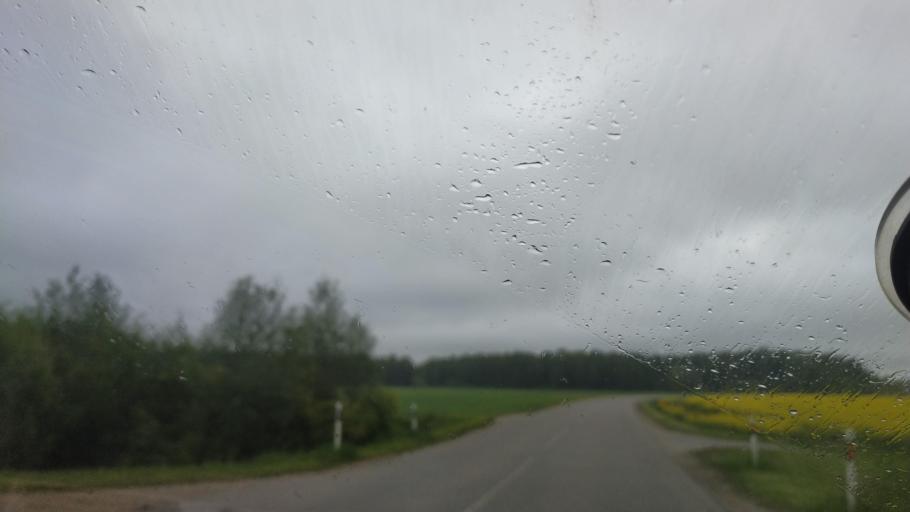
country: LT
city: Vabalninkas
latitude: 55.9993
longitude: 24.5989
